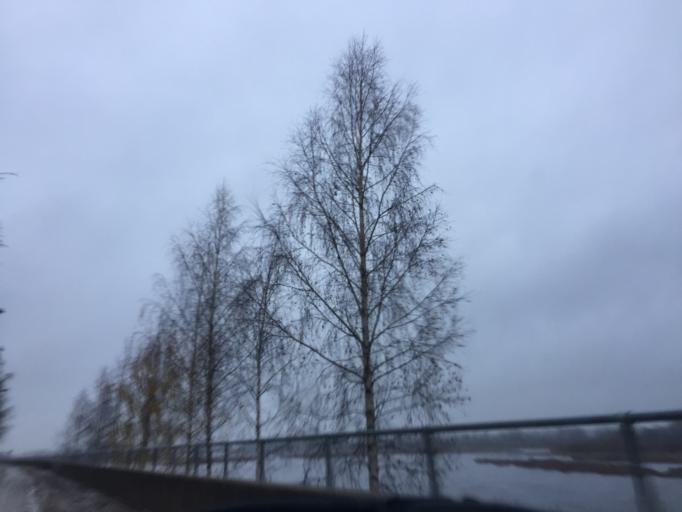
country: LV
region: Jekabpils Rajons
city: Jekabpils
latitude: 56.5066
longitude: 25.8463
